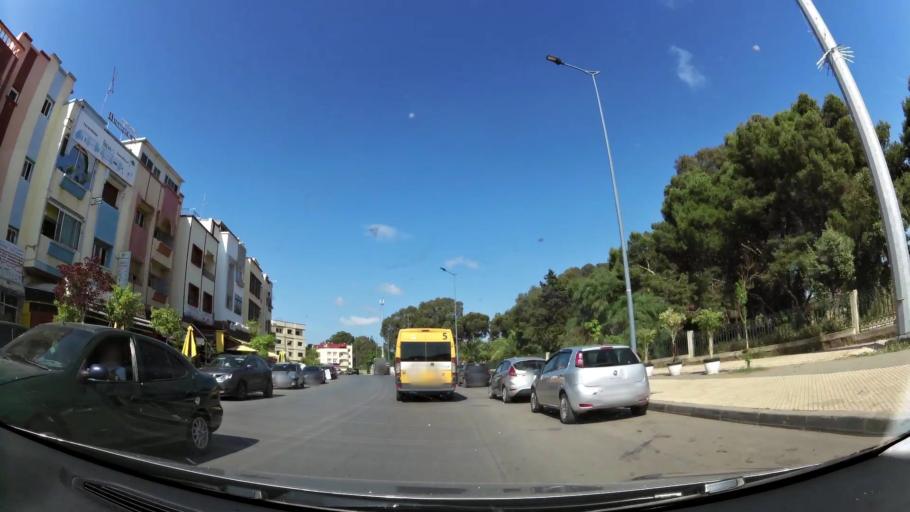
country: MA
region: Rabat-Sale-Zemmour-Zaer
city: Sale
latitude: 34.0395
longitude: -6.7810
